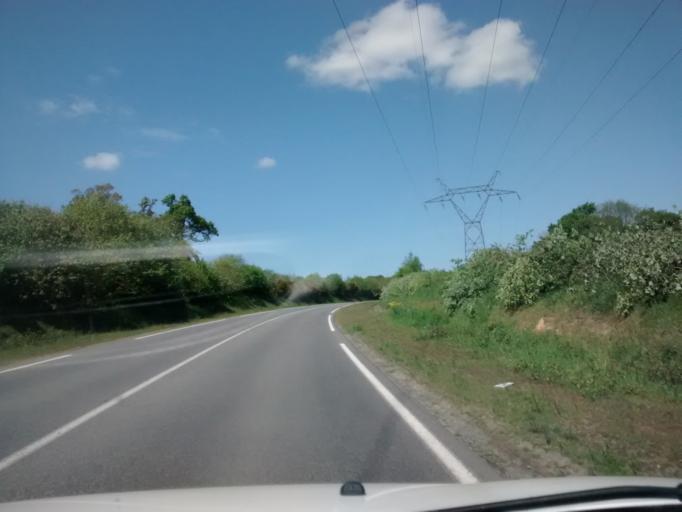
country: FR
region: Brittany
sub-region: Departement des Cotes-d'Armor
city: Pleslin-Trigavou
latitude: 48.5240
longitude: -2.0413
